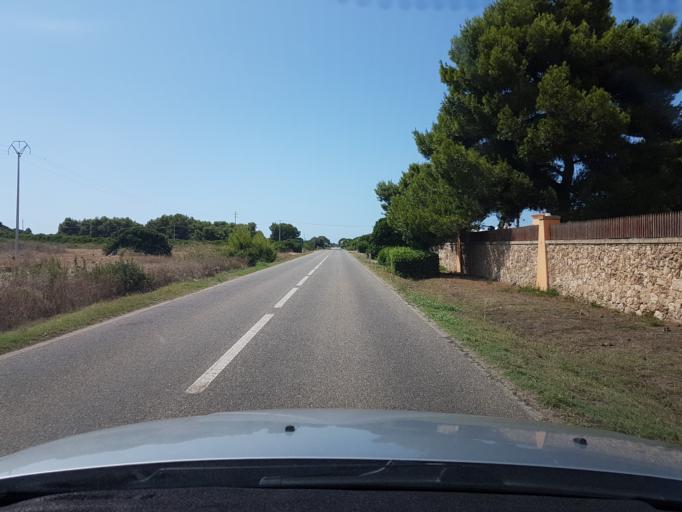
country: IT
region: Sardinia
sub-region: Provincia di Oristano
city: Riola Sardo
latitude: 40.0220
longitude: 8.4516
